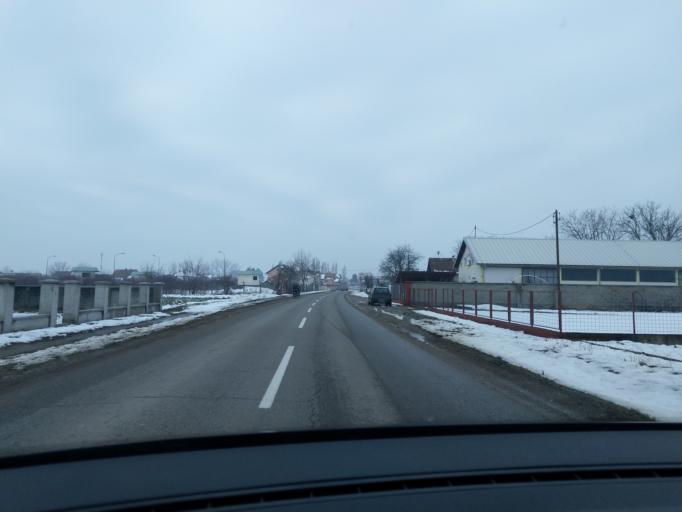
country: BA
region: Republika Srpska
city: Velika Obarska
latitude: 44.7972
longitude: 19.1740
